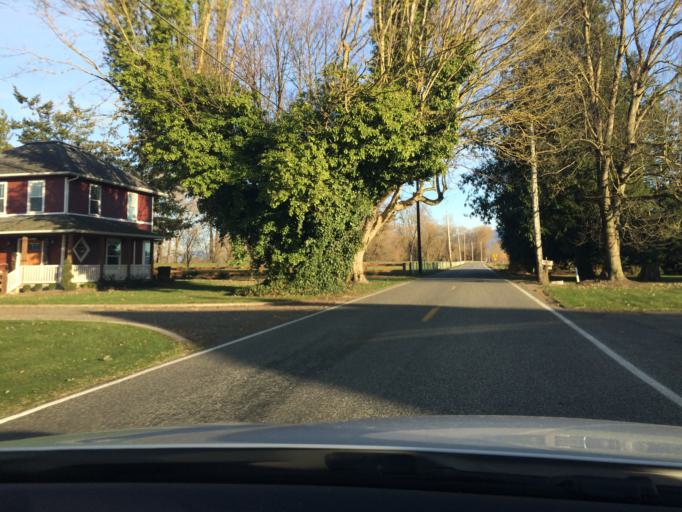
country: US
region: Washington
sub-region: Whatcom County
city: Lynden
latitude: 48.9277
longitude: -122.4082
